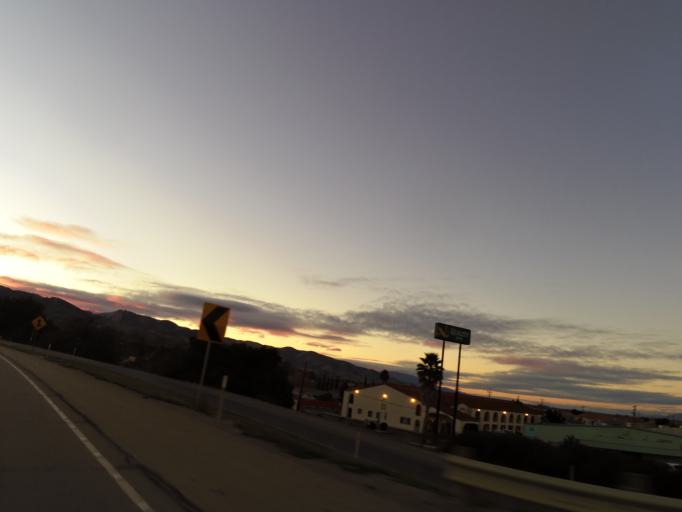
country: US
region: California
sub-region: Monterey County
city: King City
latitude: 36.2046
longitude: -121.1383
